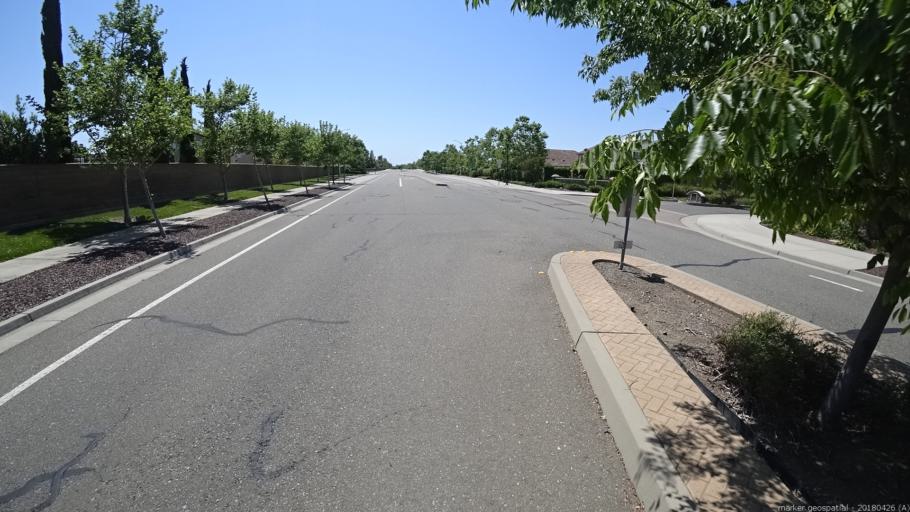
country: US
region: California
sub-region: Yolo County
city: West Sacramento
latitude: 38.5301
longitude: -121.5761
